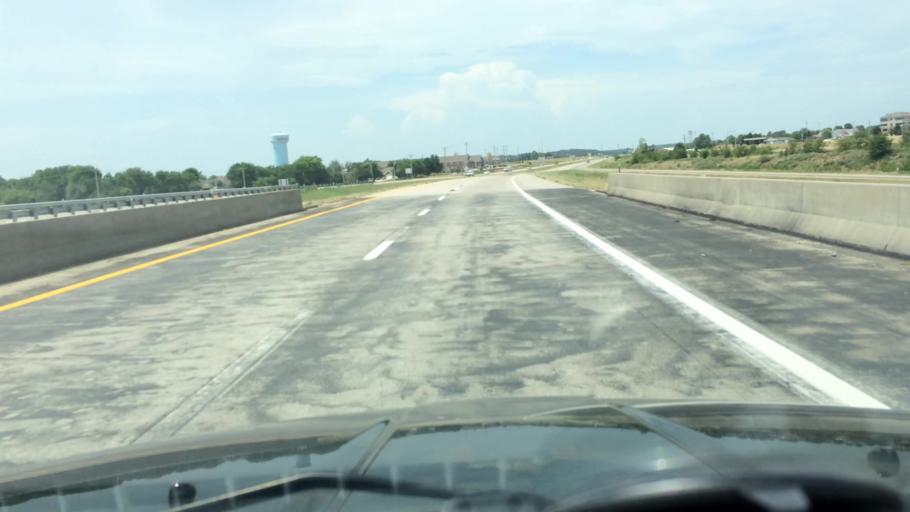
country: US
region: Missouri
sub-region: Polk County
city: Bolivar
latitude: 37.5931
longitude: -93.4322
